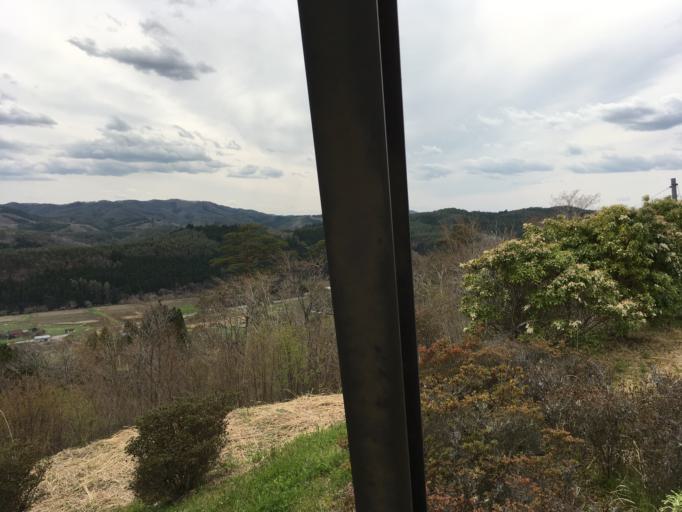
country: JP
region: Iwate
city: Ichinoseki
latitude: 38.7952
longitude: 141.4050
